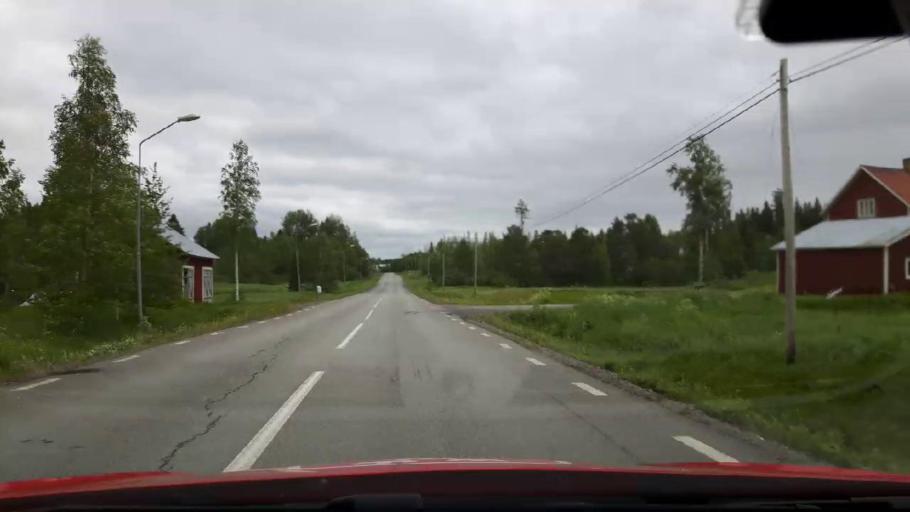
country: SE
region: Jaemtland
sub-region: OEstersunds Kommun
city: Lit
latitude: 63.6781
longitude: 15.0476
